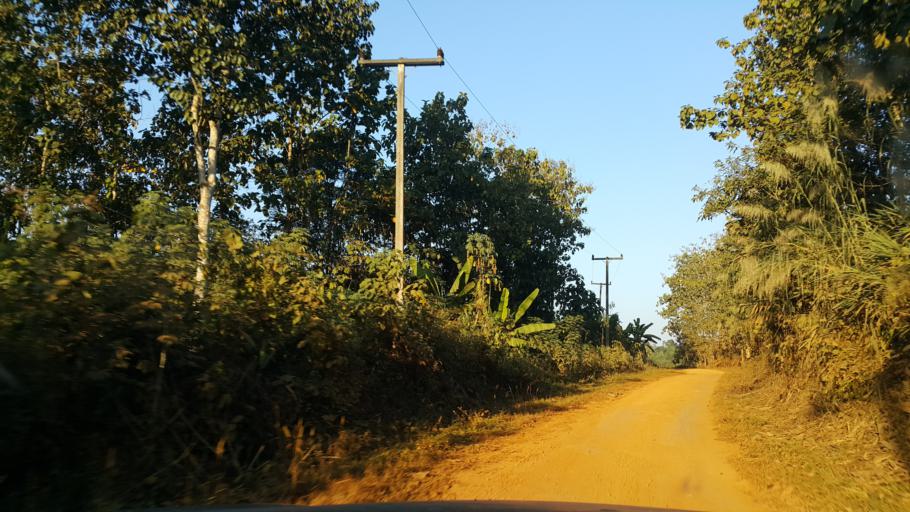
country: TH
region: Sukhothai
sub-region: Amphoe Si Satchanalai
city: Si Satchanalai
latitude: 17.6111
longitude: 99.6201
